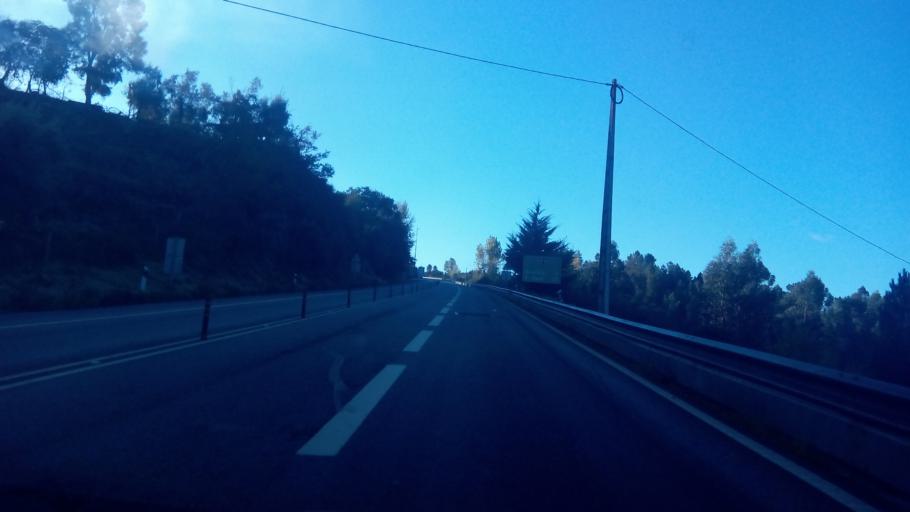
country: PT
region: Porto
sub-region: Amarante
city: Amarante
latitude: 41.2775
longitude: -7.9919
